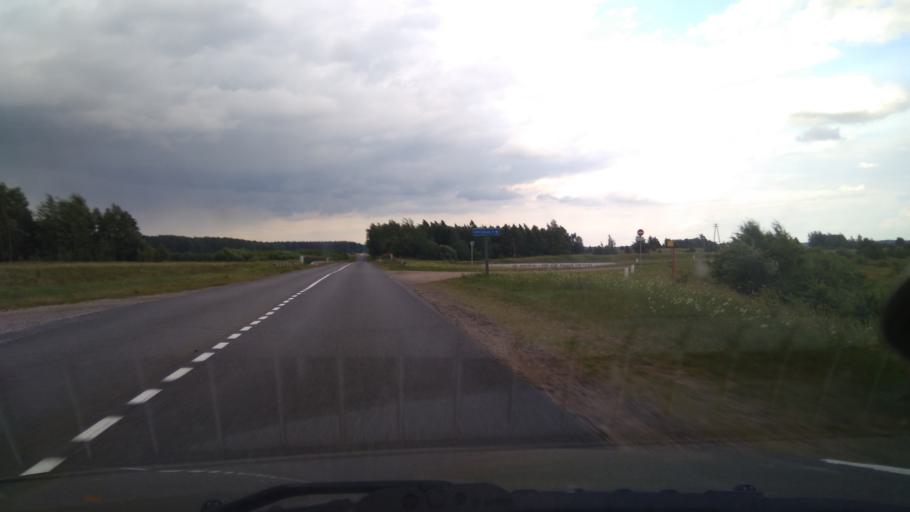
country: BY
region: Minsk
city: Il'ya
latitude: 54.4281
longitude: 27.1937
